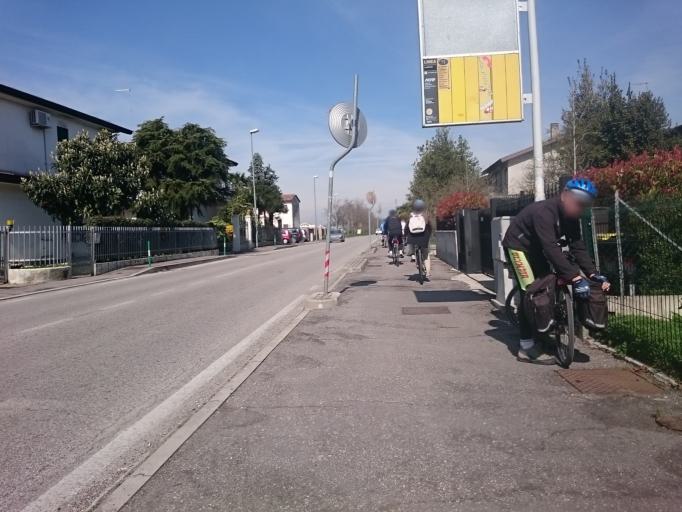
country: IT
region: Veneto
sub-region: Provincia di Padova
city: Villaguattera
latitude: 45.4394
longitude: 11.8354
